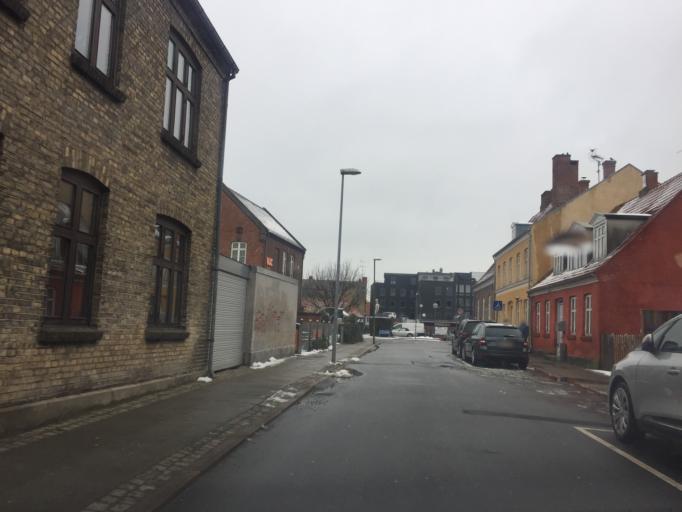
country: DK
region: Zealand
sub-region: Roskilde Kommune
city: Roskilde
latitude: 55.6396
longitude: 12.0831
